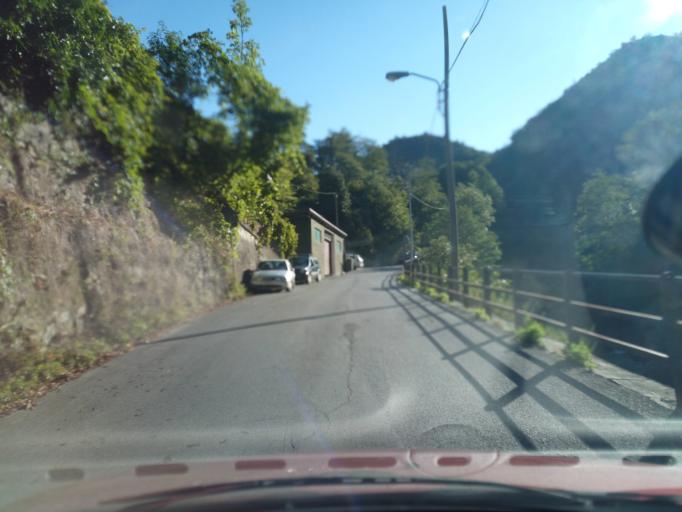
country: IT
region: Liguria
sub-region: Provincia di Genova
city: Isoverde
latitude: 44.4636
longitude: 8.8252
